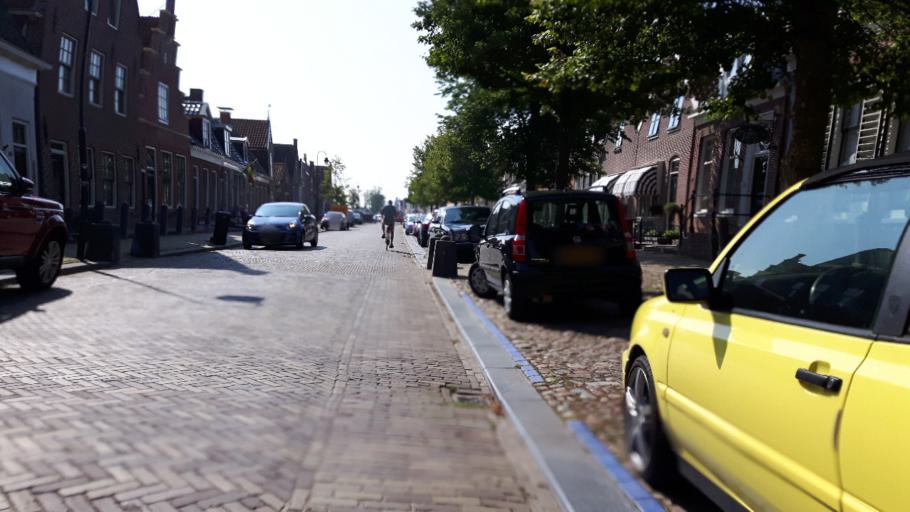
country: NL
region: Friesland
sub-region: Sudwest Fryslan
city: Workum
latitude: 52.9772
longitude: 5.4402
